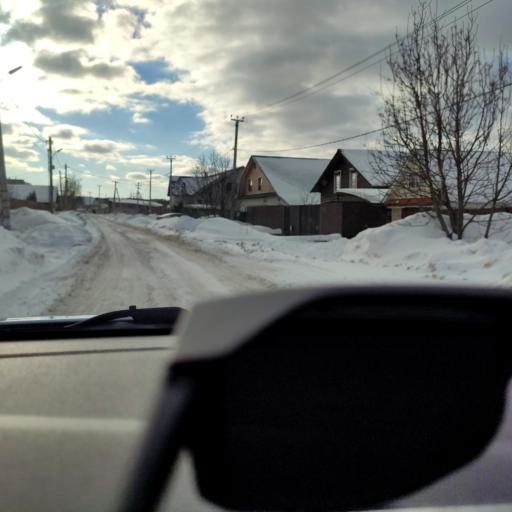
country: RU
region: Tatarstan
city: Vysokaya Gora
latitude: 55.8783
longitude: 49.2475
